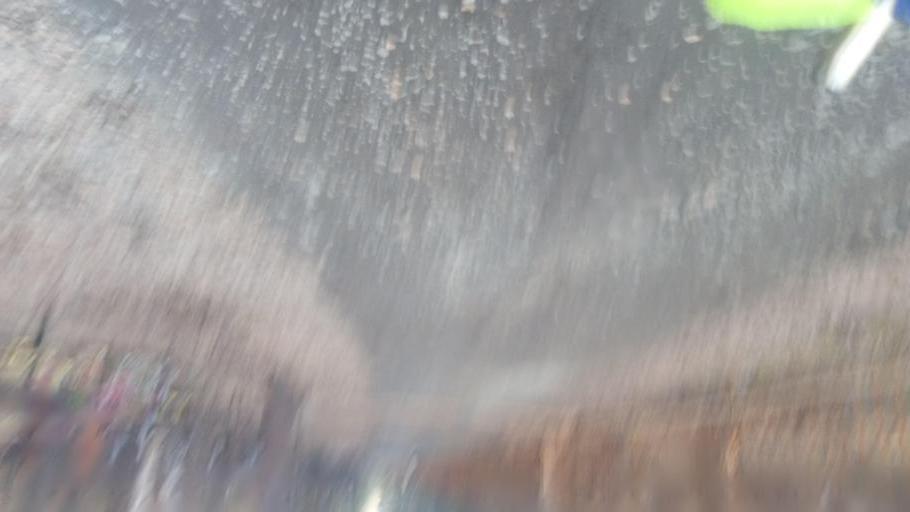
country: RU
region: Chelyabinsk
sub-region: Gorod Chelyabinsk
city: Chelyabinsk
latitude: 55.1254
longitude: 61.3463
